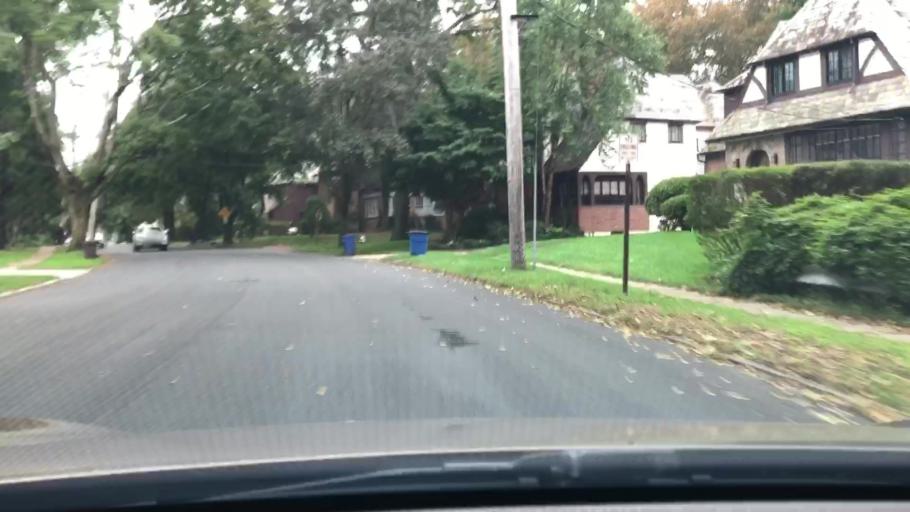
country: US
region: New York
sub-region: Westchester County
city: Bronxville
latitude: 40.9264
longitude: -73.8266
